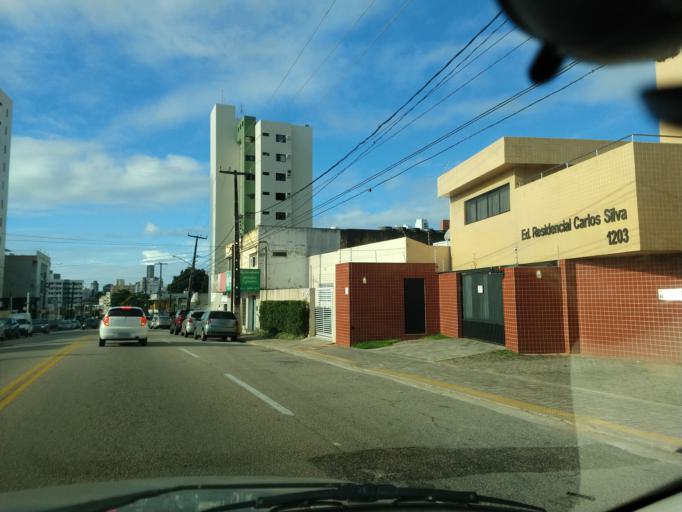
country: BR
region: Rio Grande do Norte
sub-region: Natal
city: Natal
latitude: -5.7967
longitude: -35.2098
